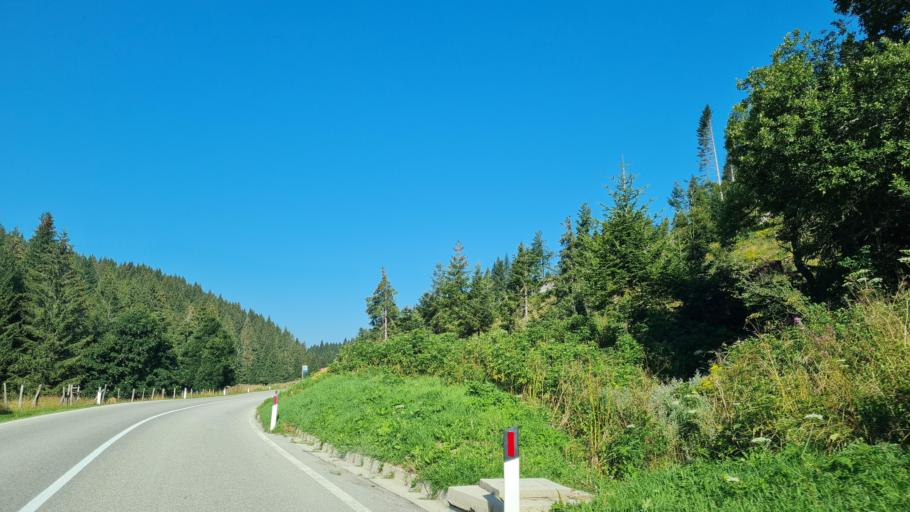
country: IT
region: Trentino-Alto Adige
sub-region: Provincia di Trento
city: Luserna
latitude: 45.9500
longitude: 11.3672
